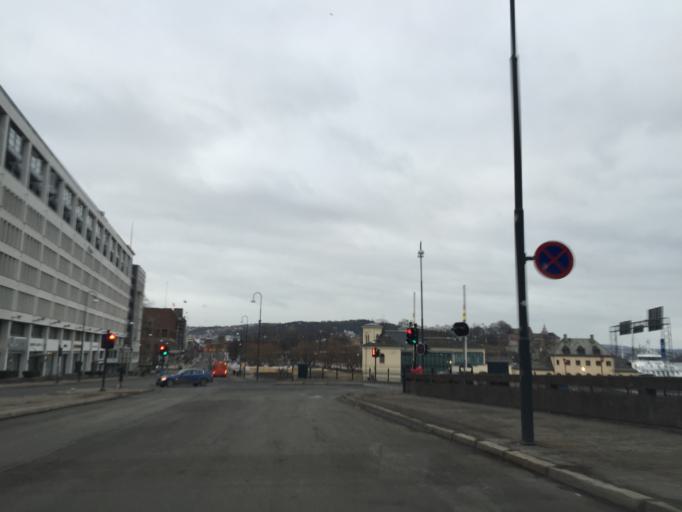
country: NO
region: Oslo
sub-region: Oslo
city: Oslo
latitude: 59.9129
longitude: 10.7279
